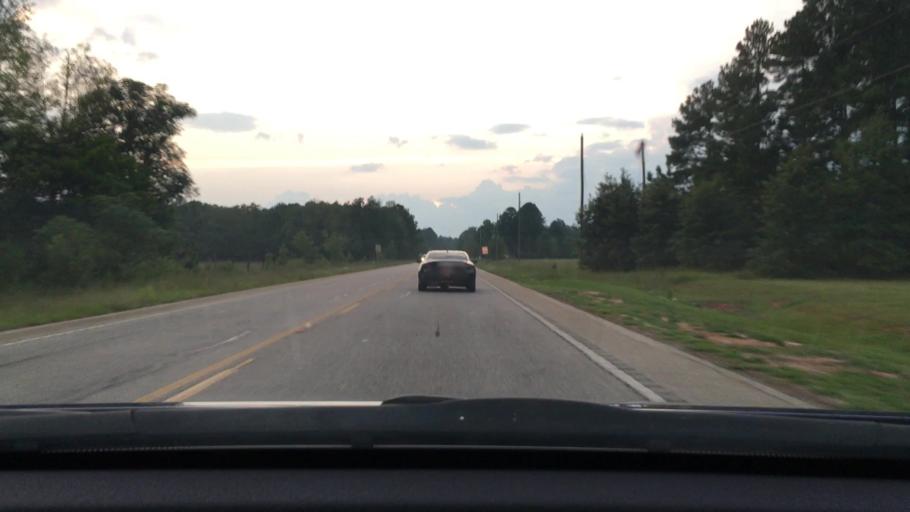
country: US
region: South Carolina
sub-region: Sumter County
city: Cherryvale
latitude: 33.9400
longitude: -80.4798
